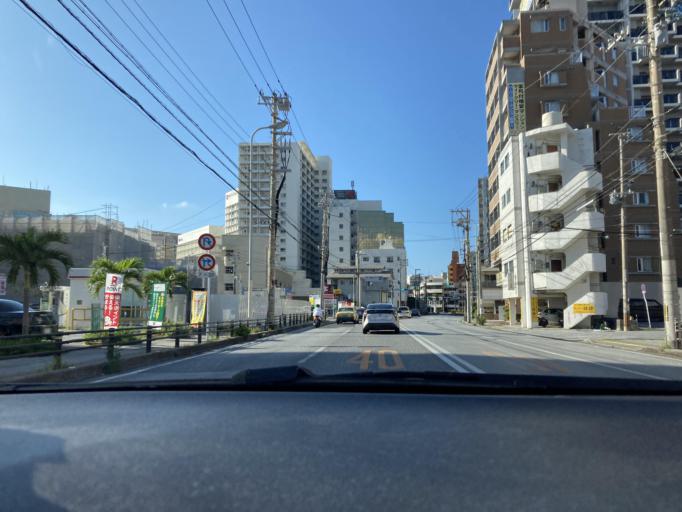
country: JP
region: Okinawa
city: Naha-shi
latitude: 26.2080
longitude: 127.6792
